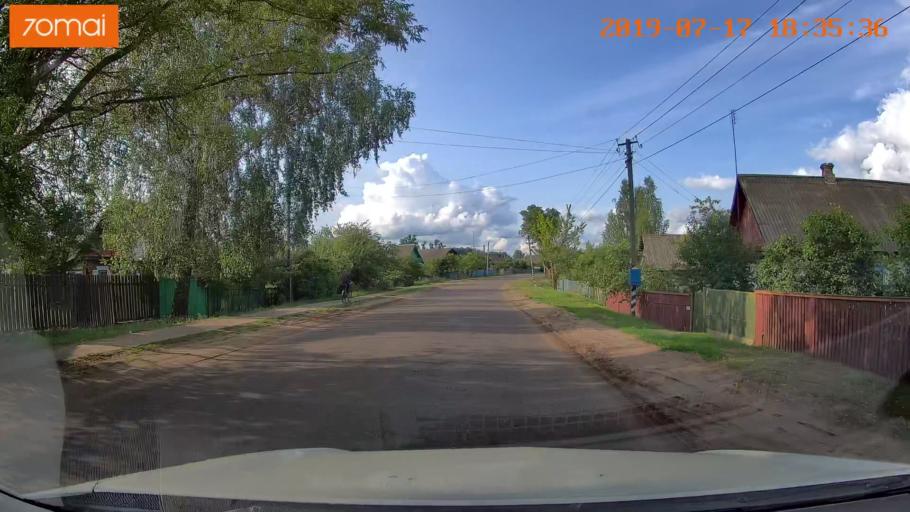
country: BY
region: Mogilev
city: Asipovichy
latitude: 53.2934
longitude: 28.6586
